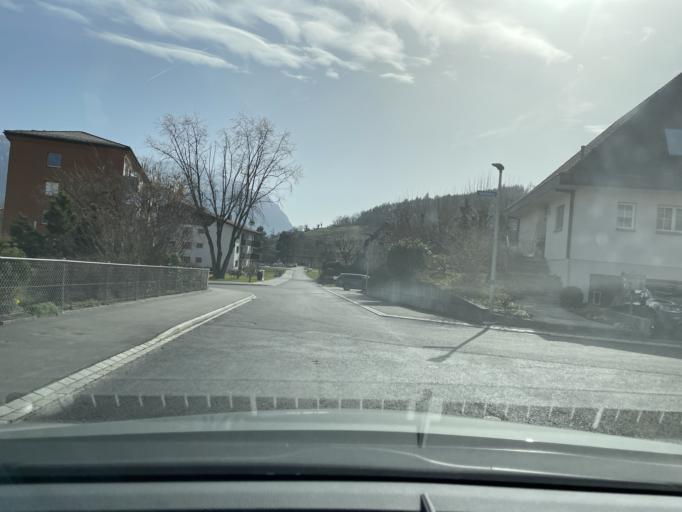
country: CH
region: Saint Gallen
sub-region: Wahlkreis Werdenberg
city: Buchs
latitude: 47.1575
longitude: 9.4741
